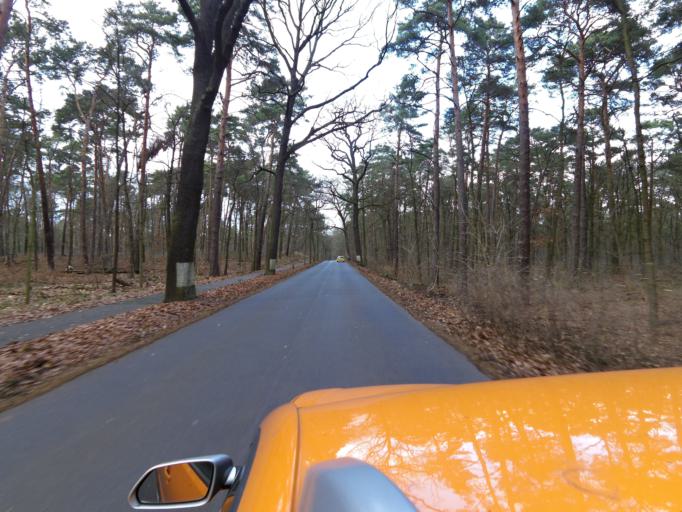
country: DE
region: Berlin
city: Nikolassee
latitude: 52.4460
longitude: 13.1976
